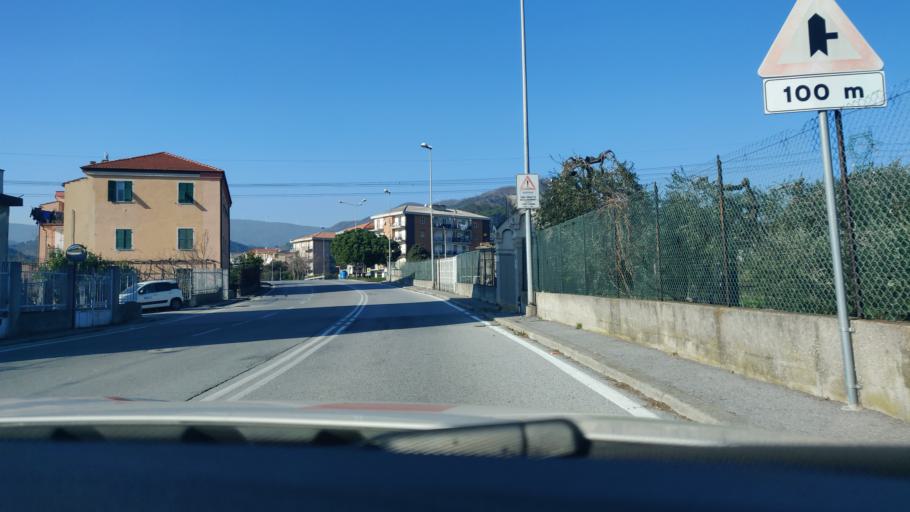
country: IT
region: Liguria
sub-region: Provincia di Savona
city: Quiliano
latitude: 44.2911
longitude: 8.4190
